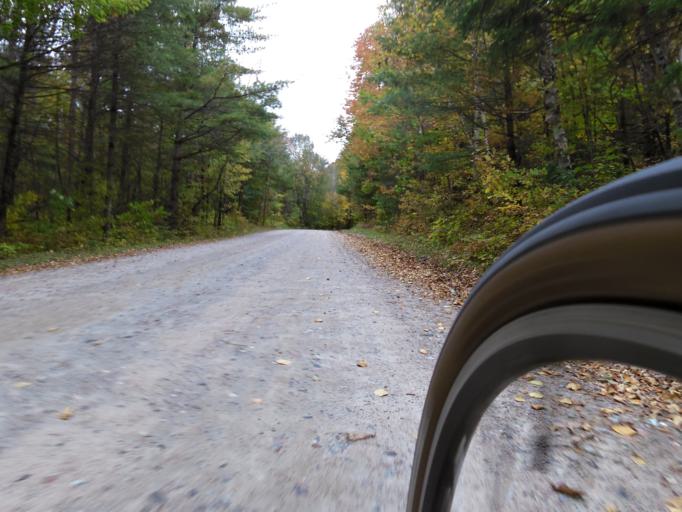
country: CA
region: Quebec
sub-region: Outaouais
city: Wakefield
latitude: 45.6040
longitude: -76.0158
